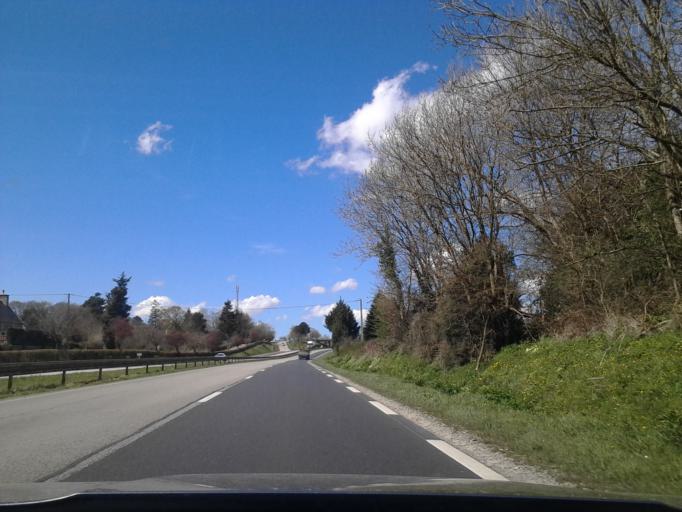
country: FR
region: Lower Normandy
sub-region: Departement de la Manche
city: Brix
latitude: 49.5320
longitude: -1.5259
